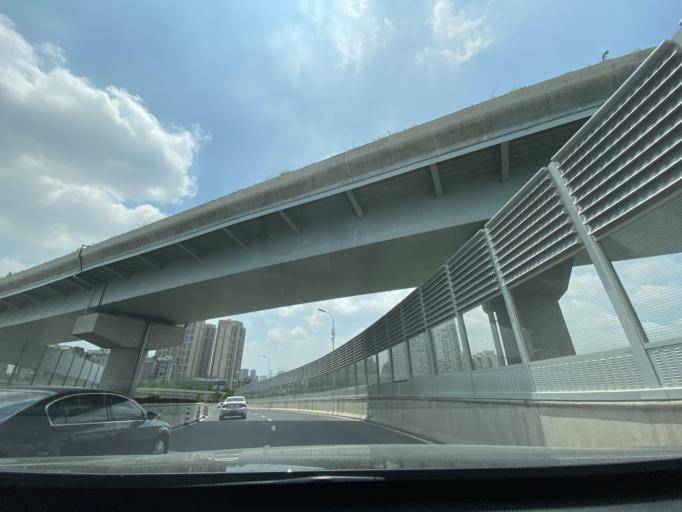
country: CN
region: Sichuan
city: Chengdu
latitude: 30.5993
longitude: 104.1067
